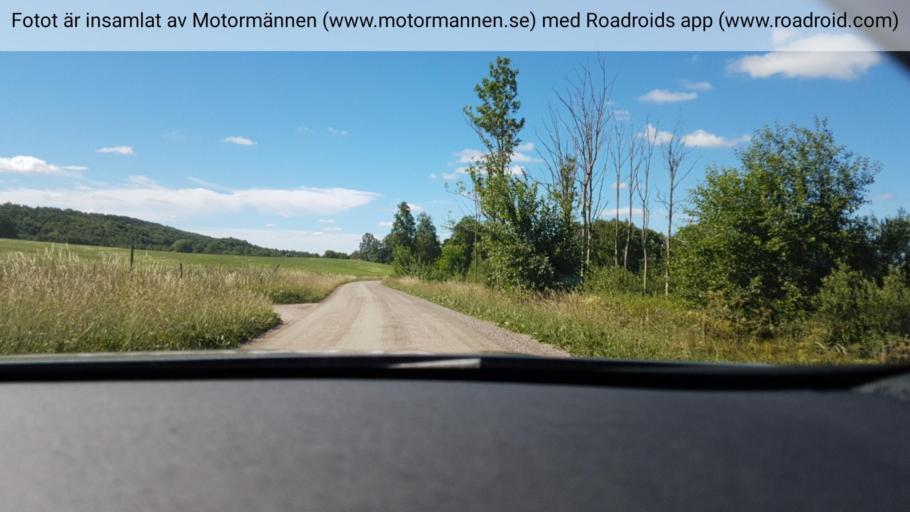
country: SE
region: Vaestra Goetaland
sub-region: Falkopings Kommun
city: Akarp
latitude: 58.1989
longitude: 13.7305
